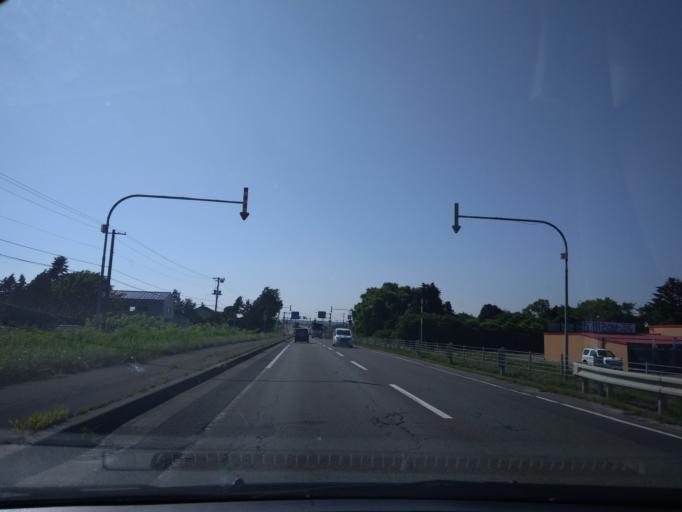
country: JP
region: Hokkaido
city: Kitahiroshima
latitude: 42.9958
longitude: 141.5922
